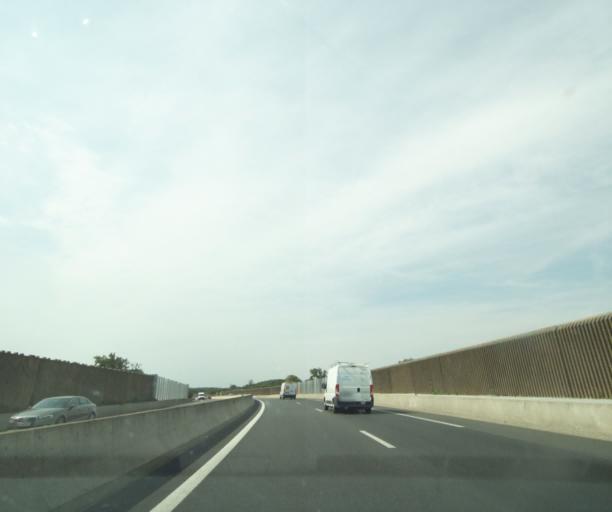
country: FR
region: Centre
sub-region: Departement d'Indre-et-Loire
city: Saint-Cyr-sur-Loire
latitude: 47.3991
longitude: 0.6478
